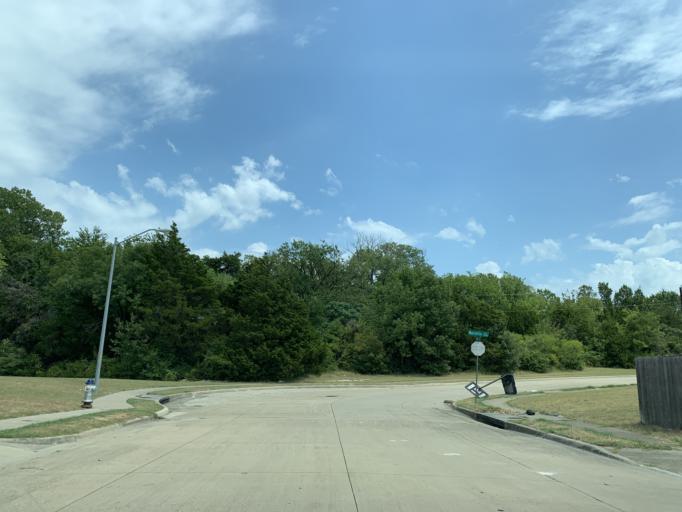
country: US
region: Texas
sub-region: Dallas County
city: DeSoto
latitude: 32.6586
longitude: -96.8150
